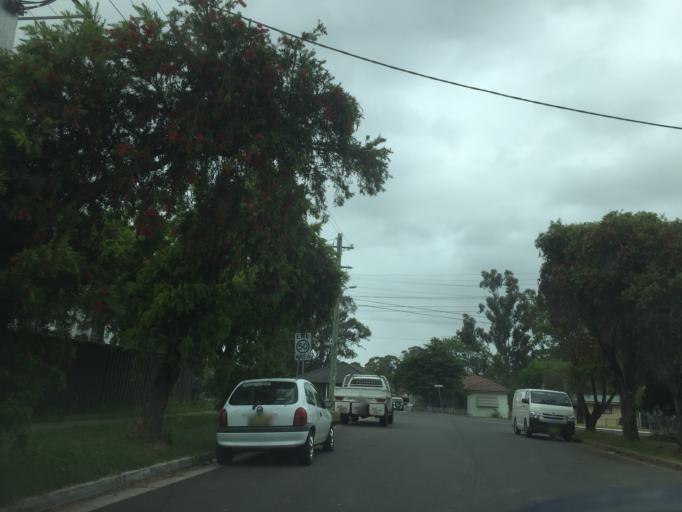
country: AU
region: New South Wales
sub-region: Blacktown
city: Blacktown
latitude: -33.7759
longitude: 150.8992
